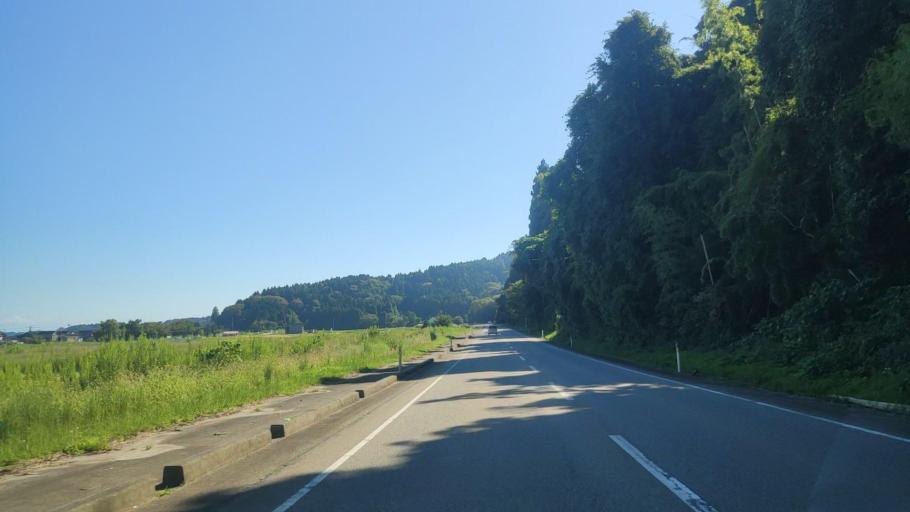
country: JP
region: Ishikawa
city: Nanao
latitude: 37.3913
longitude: 137.2340
